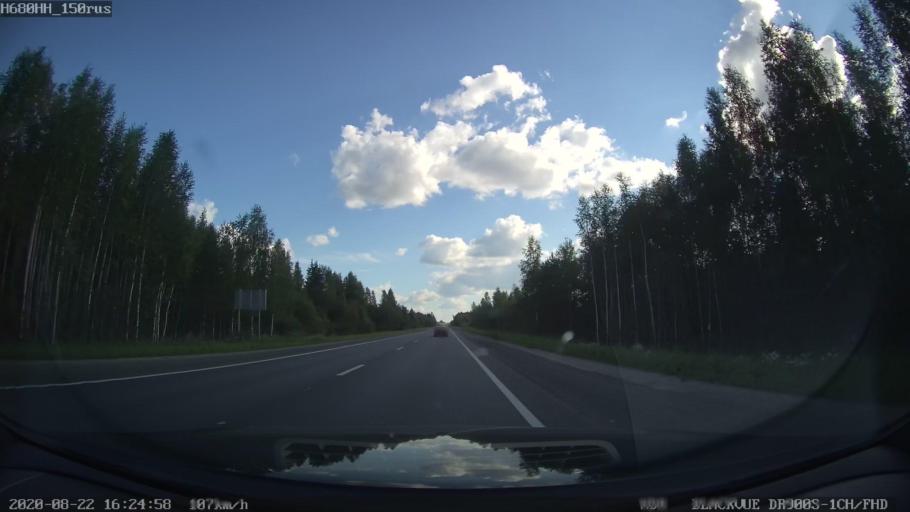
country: RU
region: Tverskaya
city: Rameshki
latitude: 57.3285
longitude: 36.0924
